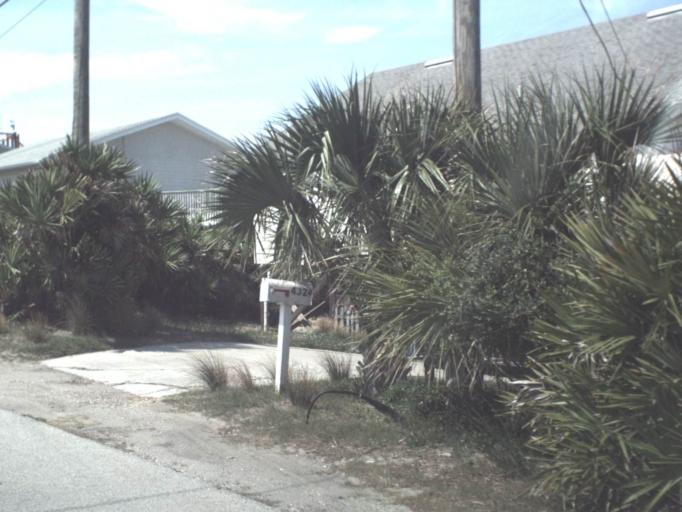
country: US
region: Florida
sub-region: Saint Johns County
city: Villano Beach
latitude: 29.9574
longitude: -81.3061
